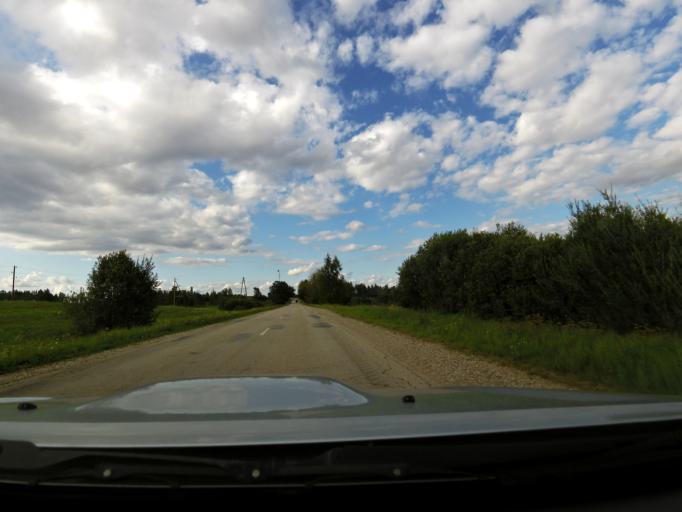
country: LV
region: Akniste
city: Akniste
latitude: 56.0459
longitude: 25.9079
